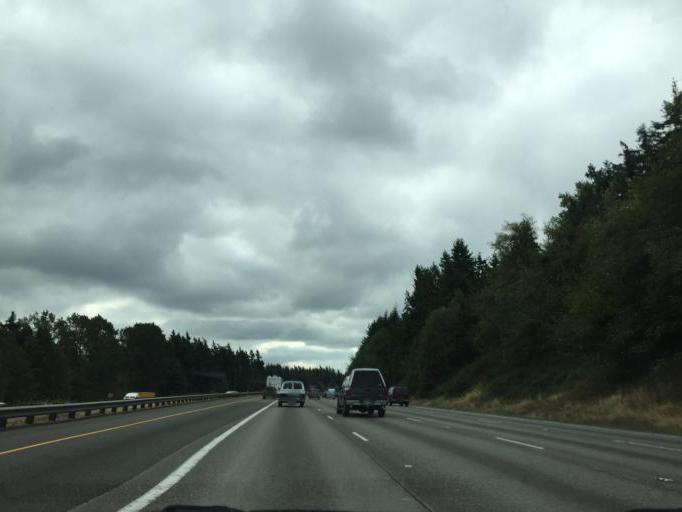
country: US
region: Washington
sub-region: King County
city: Lakeland North
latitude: 47.3496
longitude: -122.2947
